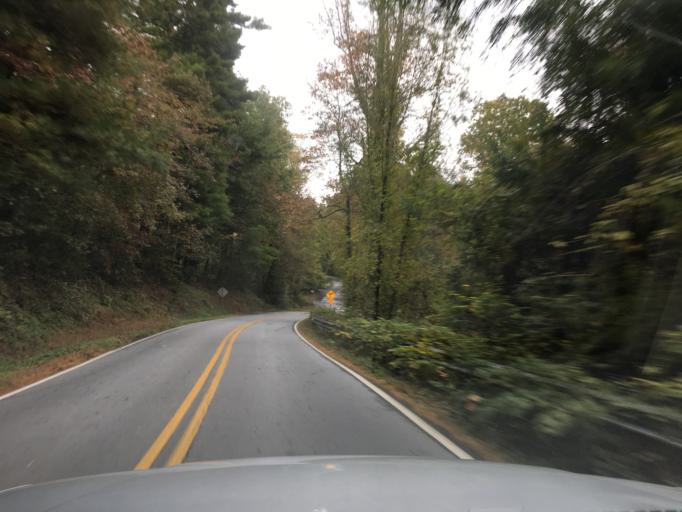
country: US
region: North Carolina
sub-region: Henderson County
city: Valley Hill
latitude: 35.2962
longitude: -82.4937
